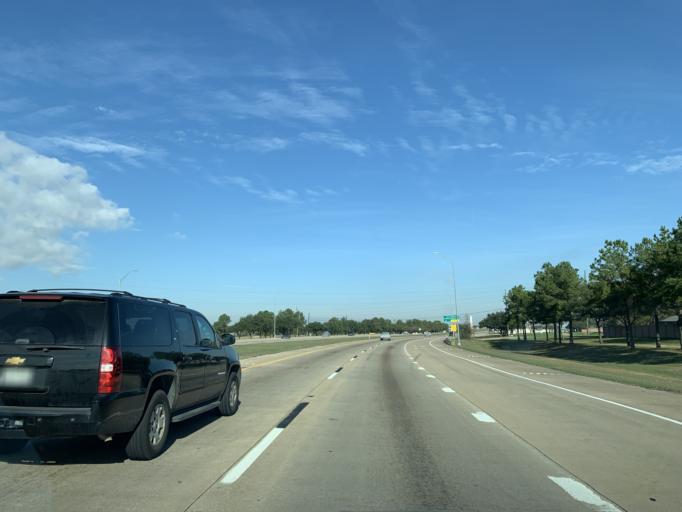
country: US
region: Texas
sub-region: Fort Bend County
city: Cinco Ranch
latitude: 29.7505
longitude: -95.7754
